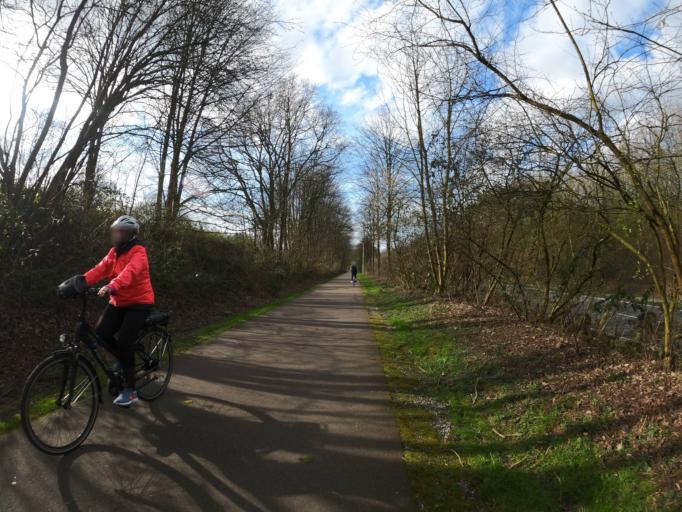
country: DE
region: North Rhine-Westphalia
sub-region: Regierungsbezirk Dusseldorf
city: Solingen
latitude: 51.2091
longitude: 7.0659
